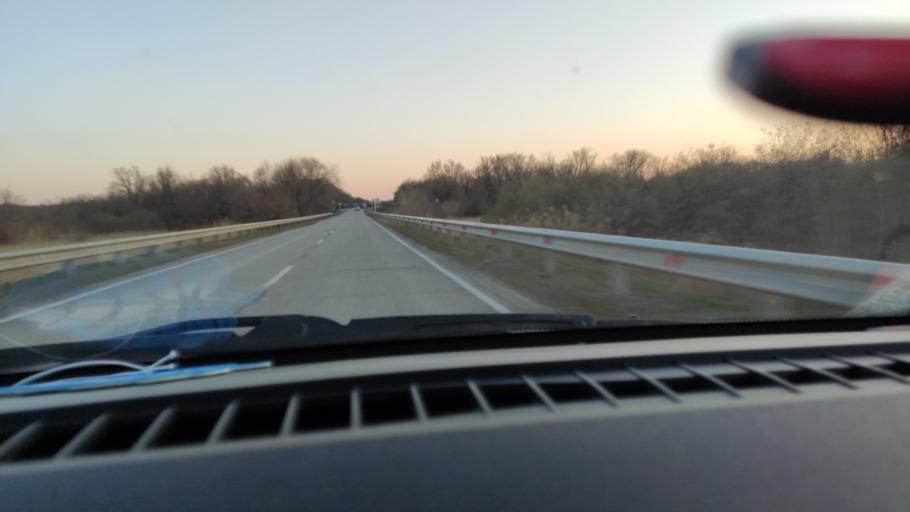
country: RU
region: Saratov
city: Privolzhskiy
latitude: 51.2472
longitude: 45.9362
